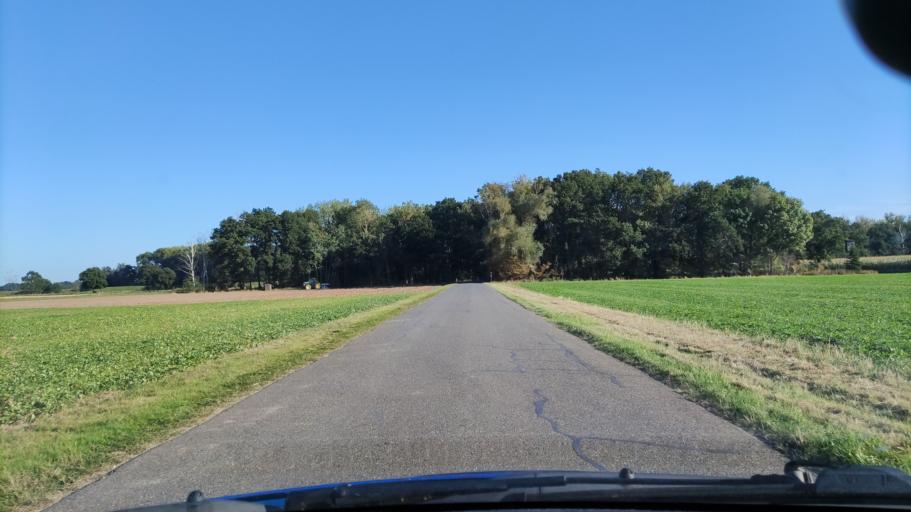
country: DE
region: Lower Saxony
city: Dannenberg
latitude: 53.1261
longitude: 11.0951
